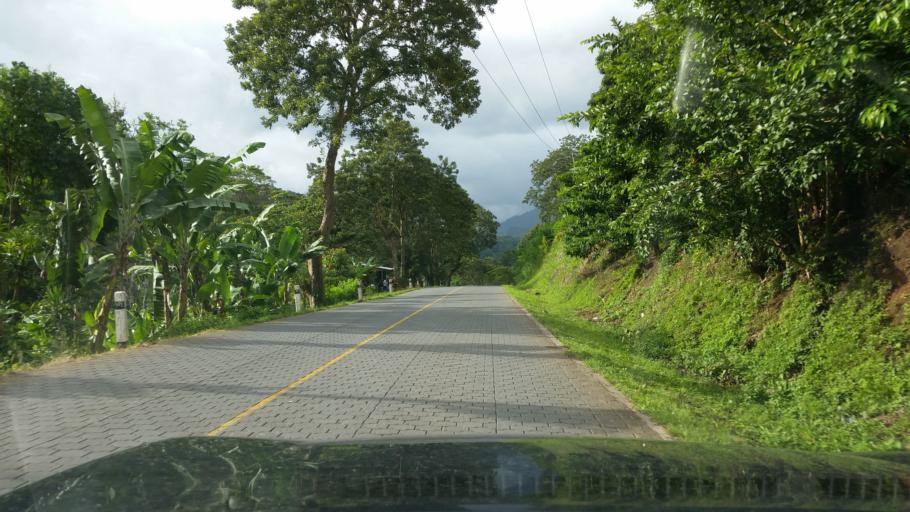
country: NI
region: Matagalpa
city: San Ramon
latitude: 13.1837
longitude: -85.7338
